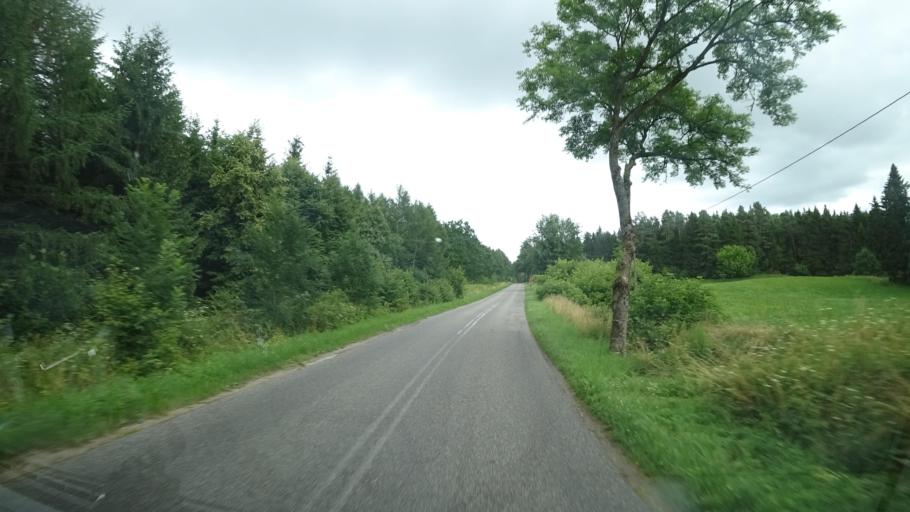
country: PL
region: Warmian-Masurian Voivodeship
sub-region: Powiat goldapski
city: Goldap
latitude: 54.3090
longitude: 22.3891
